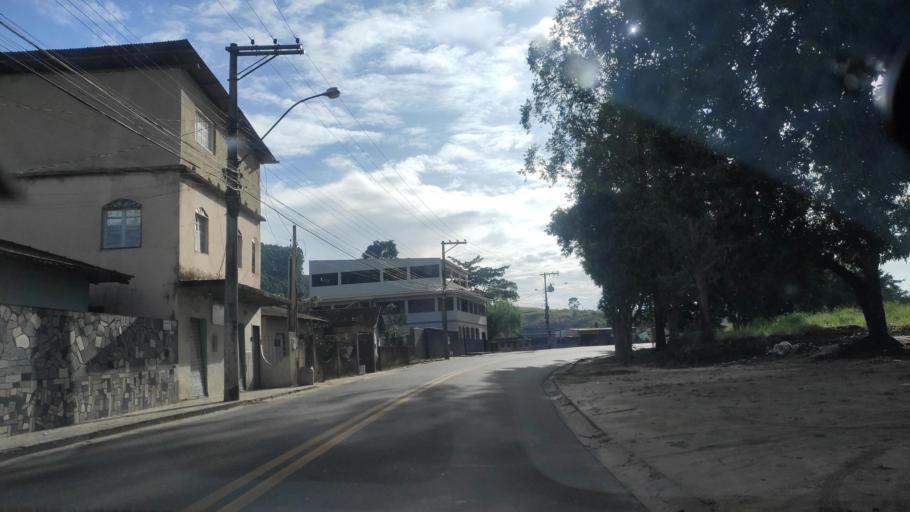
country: BR
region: Espirito Santo
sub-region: Nova Venecia
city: Nova Venecia
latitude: -18.7122
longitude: -40.3851
